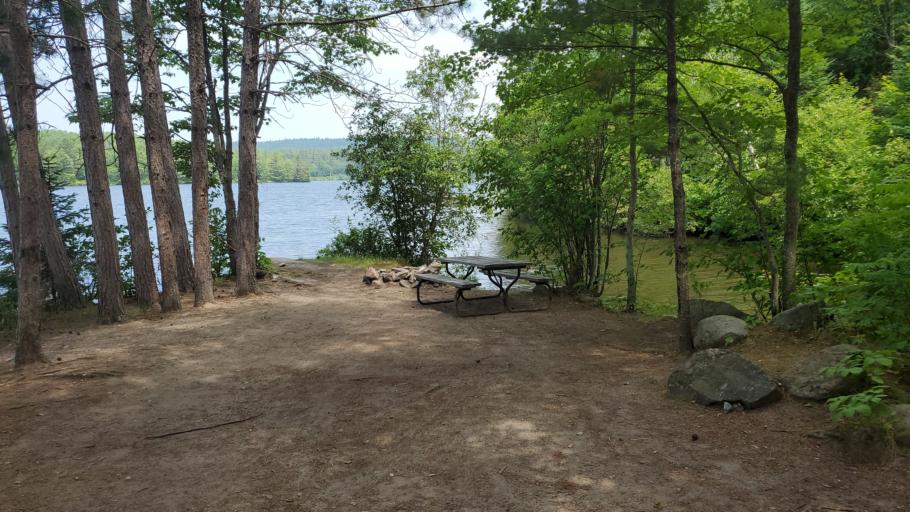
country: CA
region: Ontario
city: Mattawa
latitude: 46.2592
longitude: -78.2764
